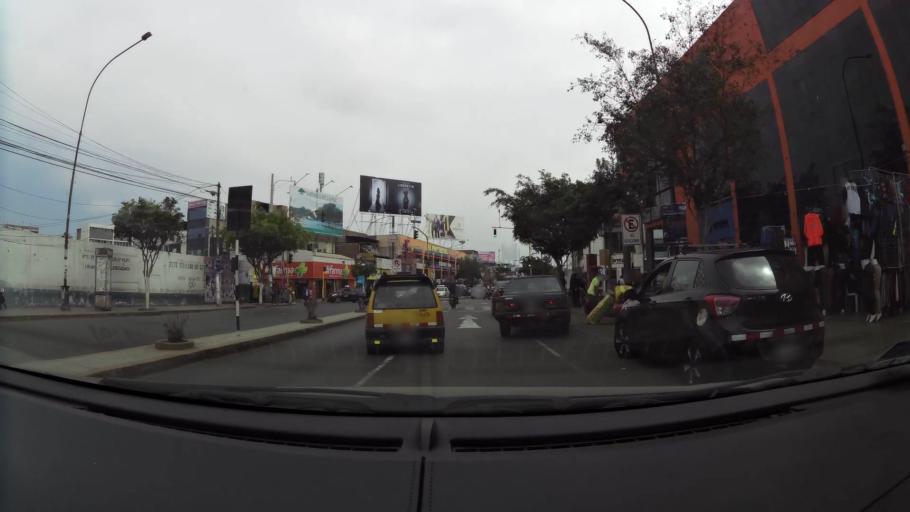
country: PE
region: La Libertad
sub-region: Provincia de Trujillo
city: Trujillo
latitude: -8.1132
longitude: -79.0236
